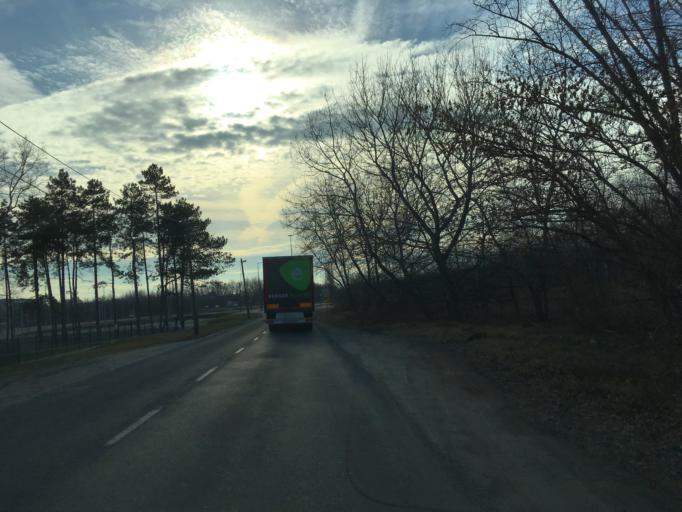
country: HU
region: Gyor-Moson-Sopron
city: Gyor
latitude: 47.7009
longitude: 17.6663
